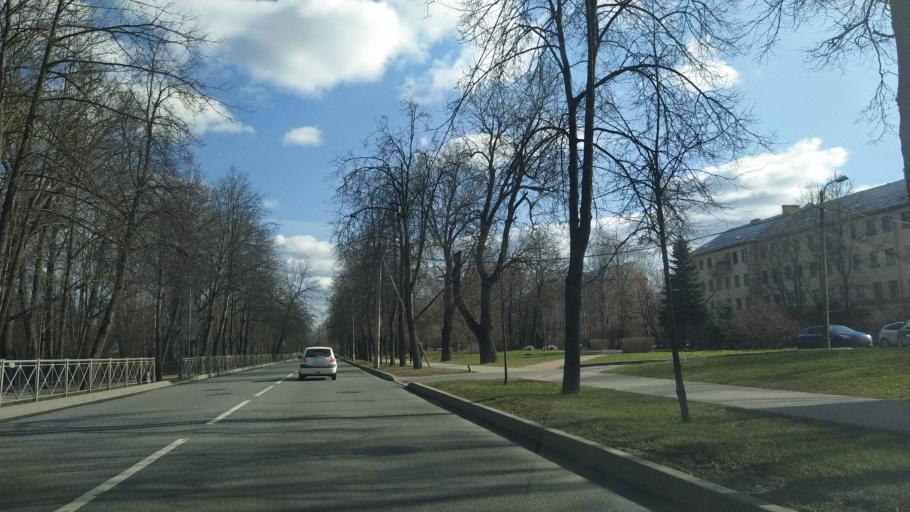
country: RU
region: St.-Petersburg
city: Pushkin
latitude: 59.7063
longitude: 30.4168
